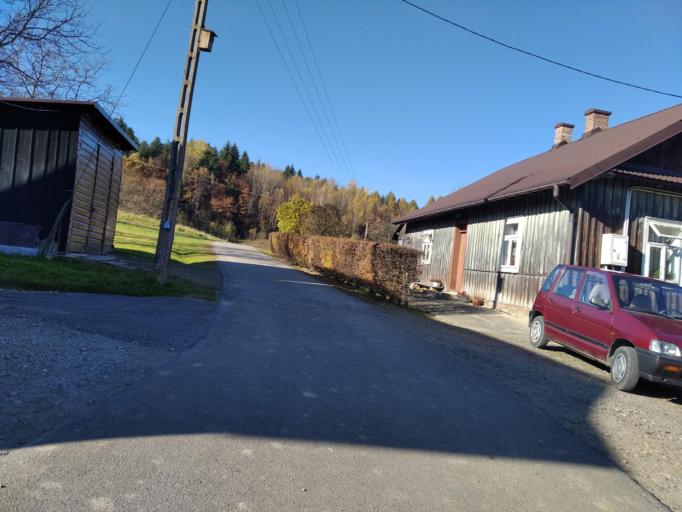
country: PL
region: Subcarpathian Voivodeship
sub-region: Powiat strzyzowski
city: Frysztak
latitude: 49.8508
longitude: 21.6028
